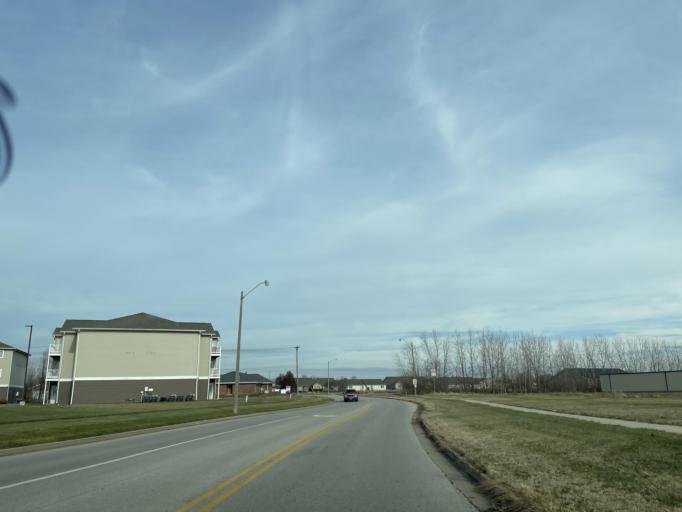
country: US
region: Illinois
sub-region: Sangamon County
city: Jerome
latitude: 39.7579
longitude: -89.7298
